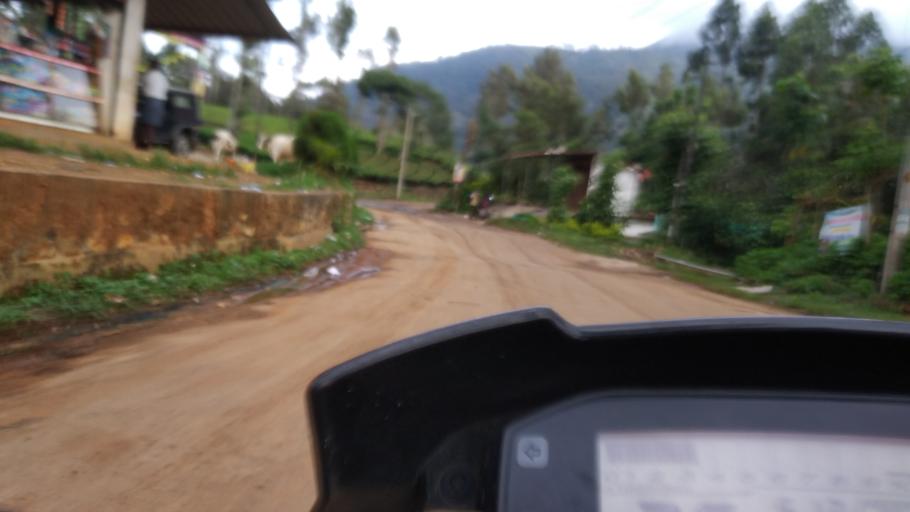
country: IN
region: Tamil Nadu
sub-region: Theni
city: Bodinayakkanur
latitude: 10.0242
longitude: 77.2397
